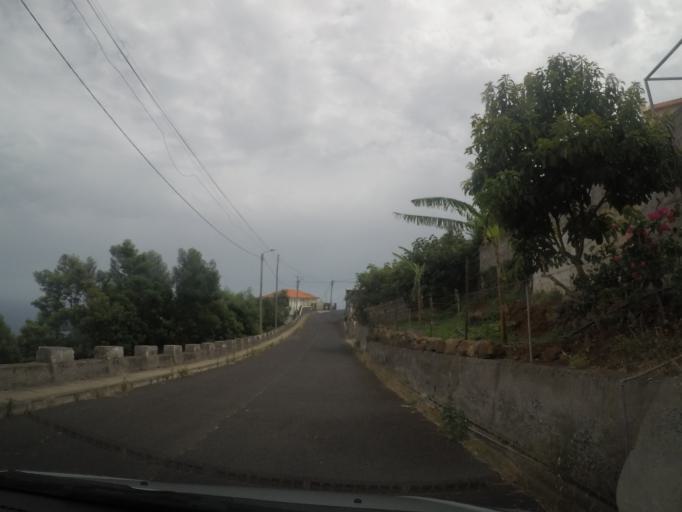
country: PT
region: Madeira
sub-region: Santa Cruz
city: Santa Cruz
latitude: 32.6803
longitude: -16.8090
